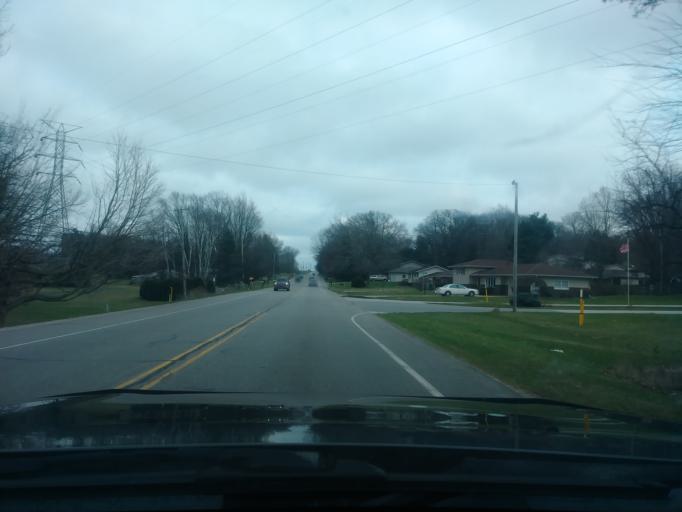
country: US
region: Indiana
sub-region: LaPorte County
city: Trail Creek
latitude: 41.6485
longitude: -86.8084
